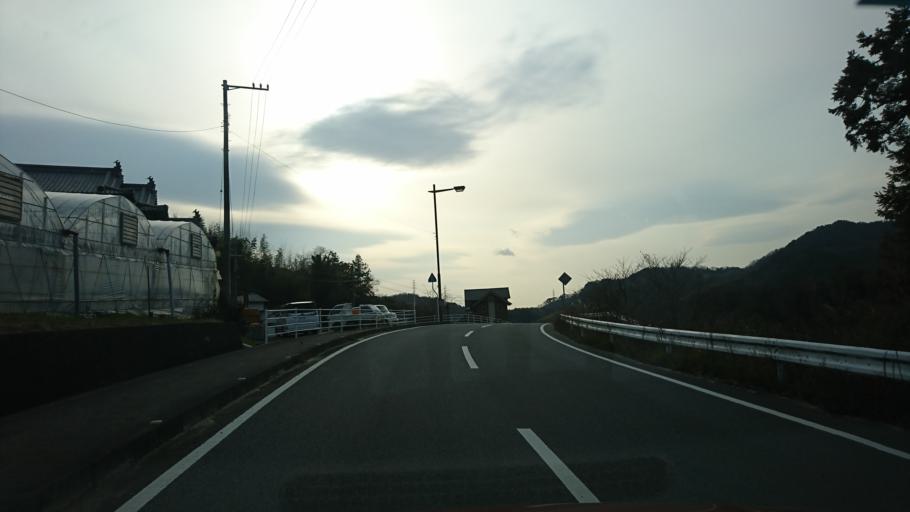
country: JP
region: Ehime
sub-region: Shikoku-chuo Shi
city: Matsuyama
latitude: 33.8906
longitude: 132.8037
